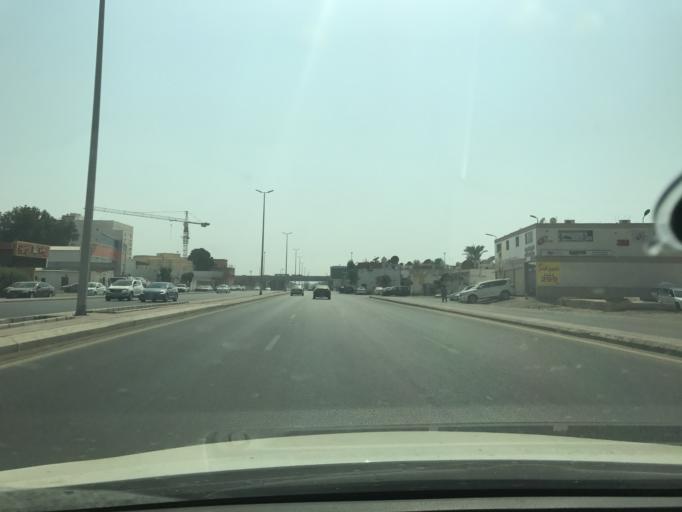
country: SA
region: Makkah
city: Jeddah
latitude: 21.6298
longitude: 39.1569
